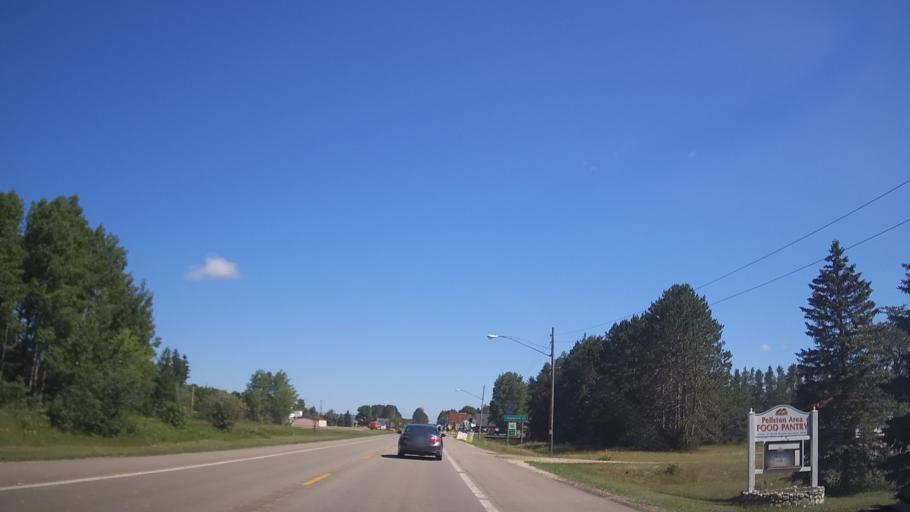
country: US
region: Michigan
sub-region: Cheboygan County
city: Indian River
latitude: 45.5484
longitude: -84.7845
